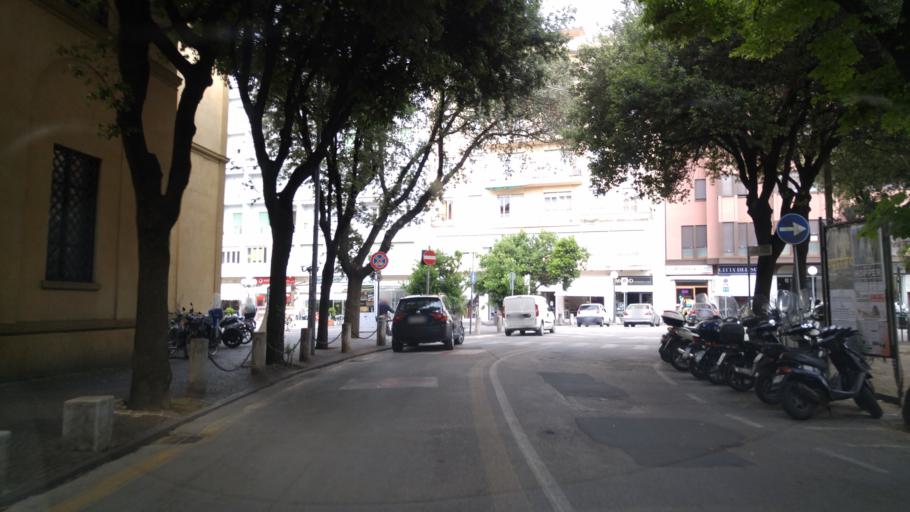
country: IT
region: The Marches
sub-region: Provincia di Pesaro e Urbino
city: Pesaro
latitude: 43.9076
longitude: 12.9088
